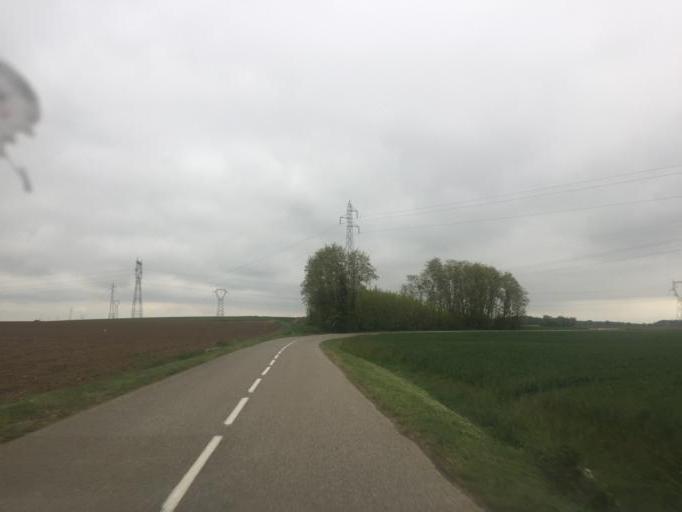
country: FR
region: Rhone-Alpes
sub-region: Departement de l'Ain
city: Beynost
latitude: 45.8621
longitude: 4.9937
